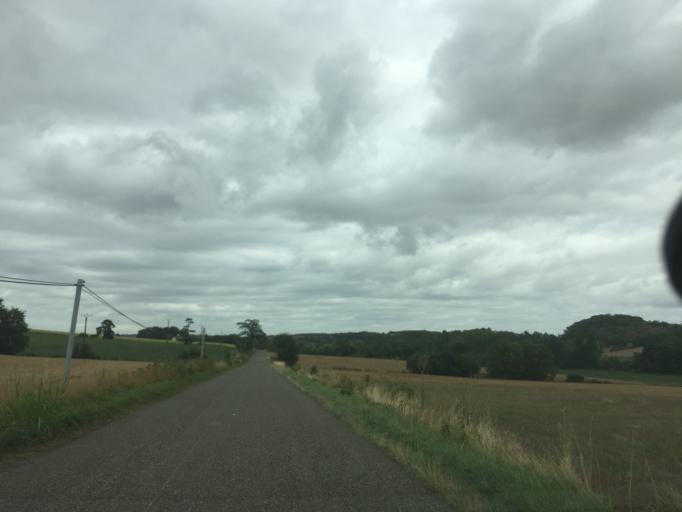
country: FR
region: Midi-Pyrenees
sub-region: Departement du Gers
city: Mirande
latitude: 43.5985
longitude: 0.3290
